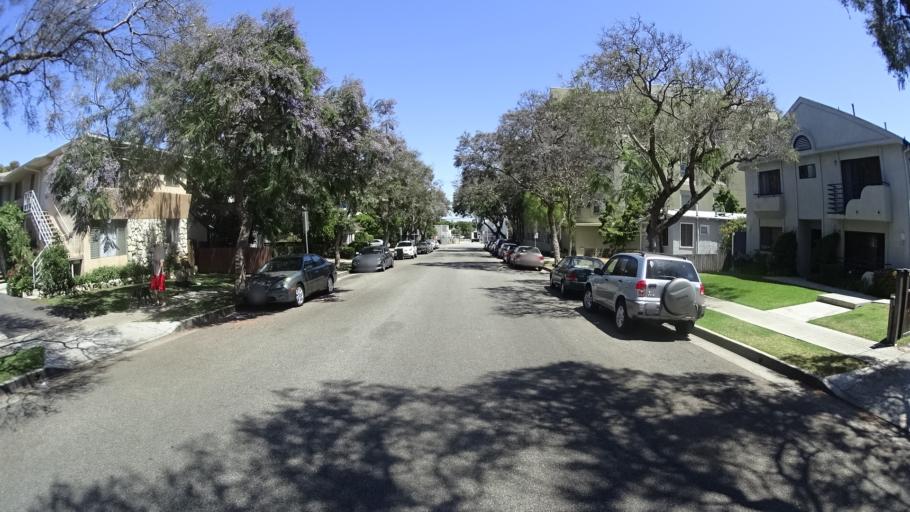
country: US
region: California
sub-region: Los Angeles County
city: Santa Monica
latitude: 34.0313
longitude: -118.4815
